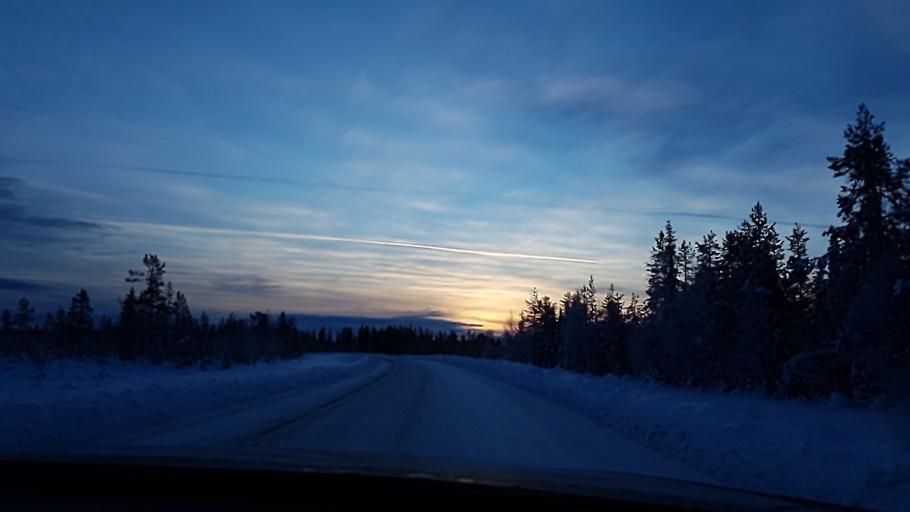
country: SE
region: Norrbotten
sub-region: Jokkmokks Kommun
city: Jokkmokk
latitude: 66.1049
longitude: 20.0567
